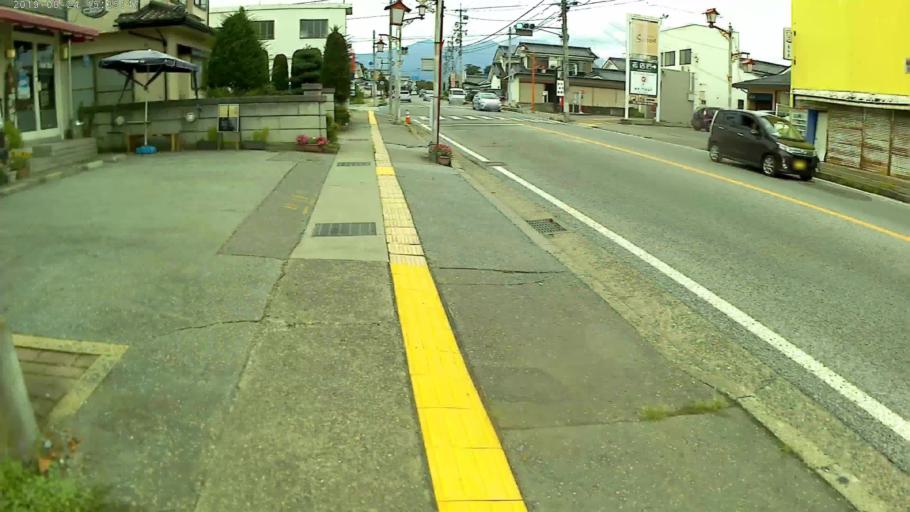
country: JP
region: Nagano
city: Saku
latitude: 36.2758
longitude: 138.4782
